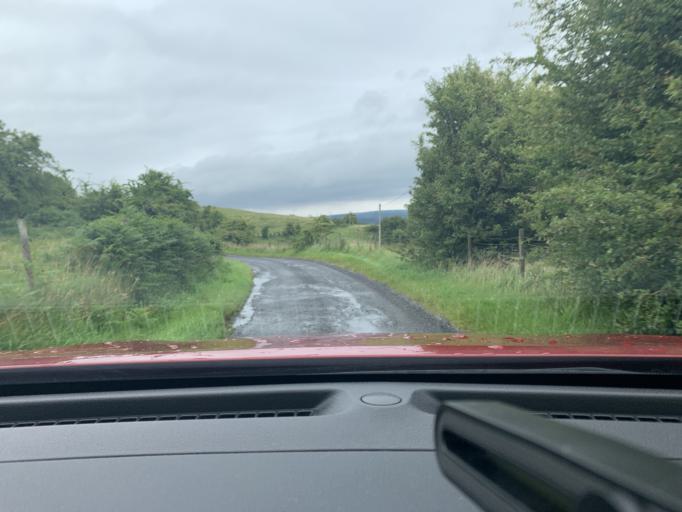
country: GB
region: Northern Ireland
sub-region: Fermanagh District
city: Enniskillen
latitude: 54.2712
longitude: -7.8545
